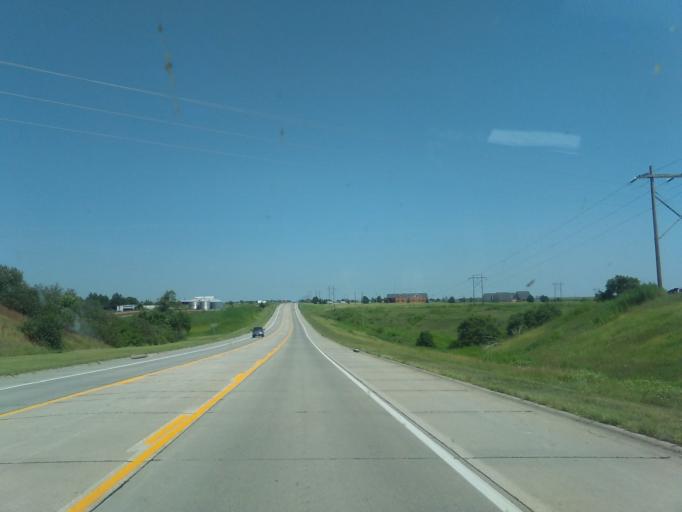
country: US
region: Nebraska
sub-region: Red Willow County
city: McCook
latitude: 40.2223
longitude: -100.6500
